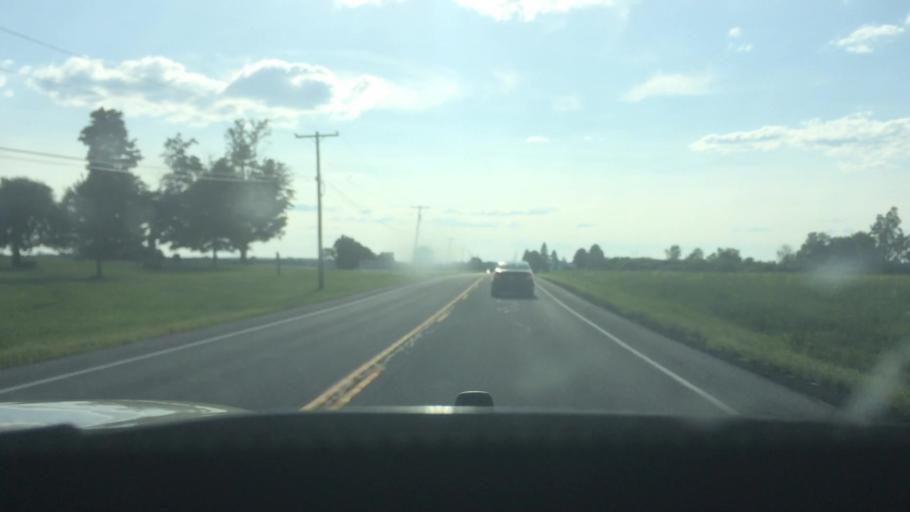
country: US
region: New York
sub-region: St. Lawrence County
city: Potsdam
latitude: 44.6889
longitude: -74.7568
